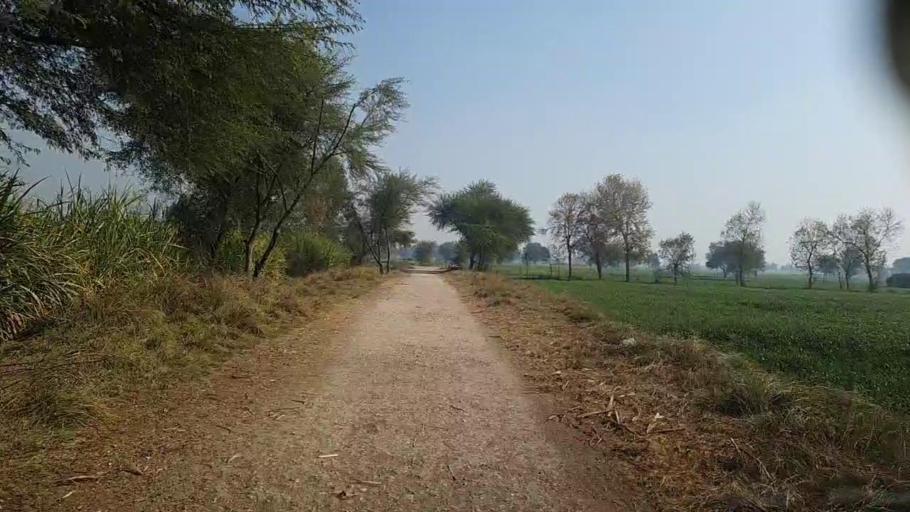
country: PK
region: Sindh
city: Khairpur
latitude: 27.9333
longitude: 69.6689
